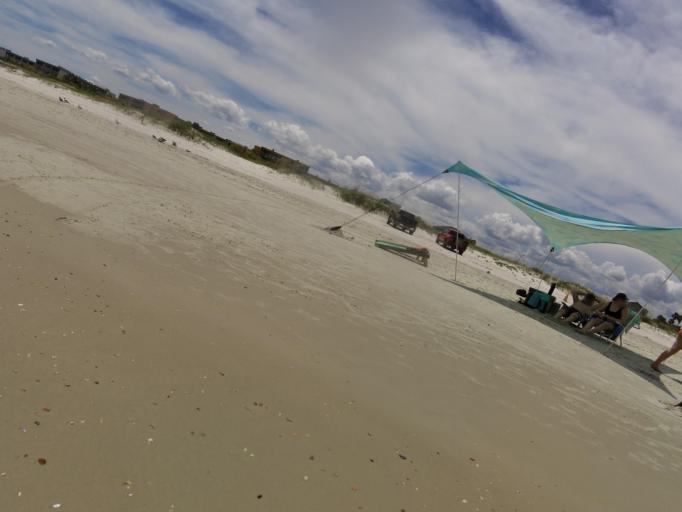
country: US
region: Florida
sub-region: Saint Johns County
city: Butler Beach
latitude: 29.8242
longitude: -81.2624
